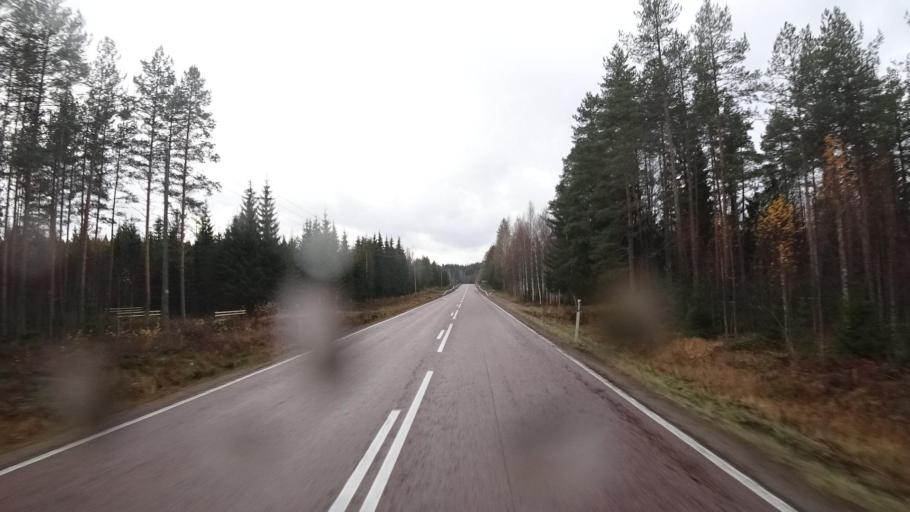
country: FI
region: Southern Savonia
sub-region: Mikkeli
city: Kangasniemi
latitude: 62.0681
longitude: 26.6625
